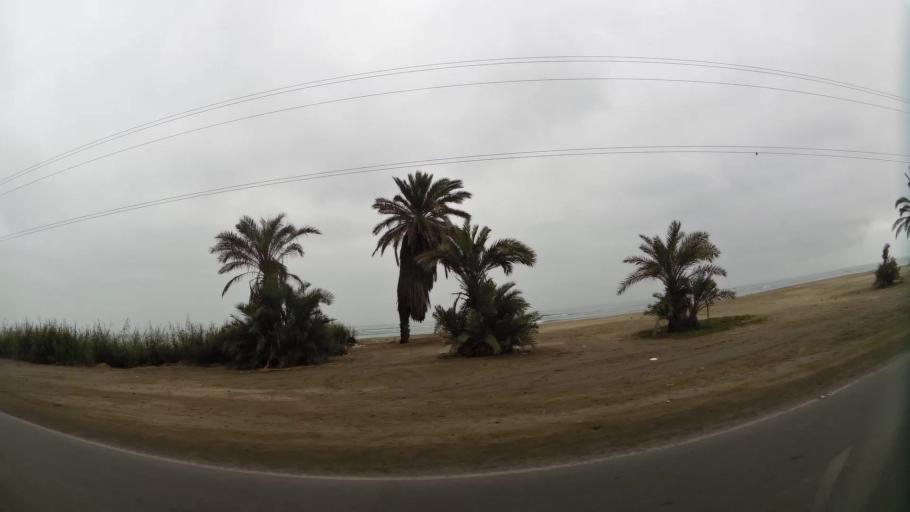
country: PE
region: Ica
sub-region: Provincia de Pisco
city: Pisco
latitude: -13.7233
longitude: -76.2218
